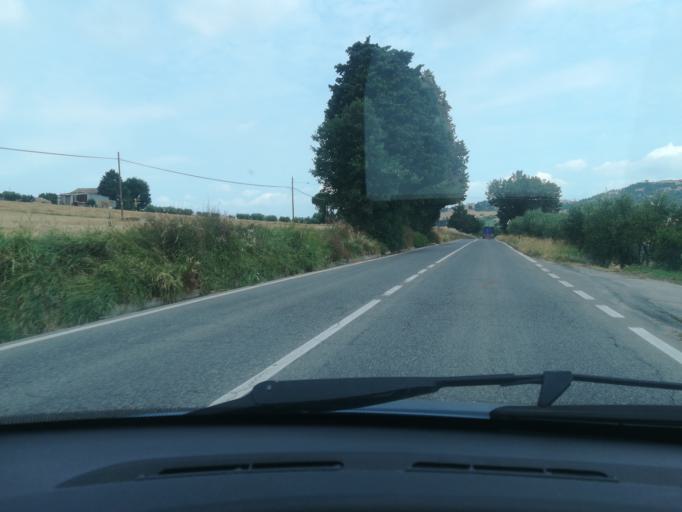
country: IT
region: The Marches
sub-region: Provincia di Macerata
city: Recanati
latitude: 43.3817
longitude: 13.5369
